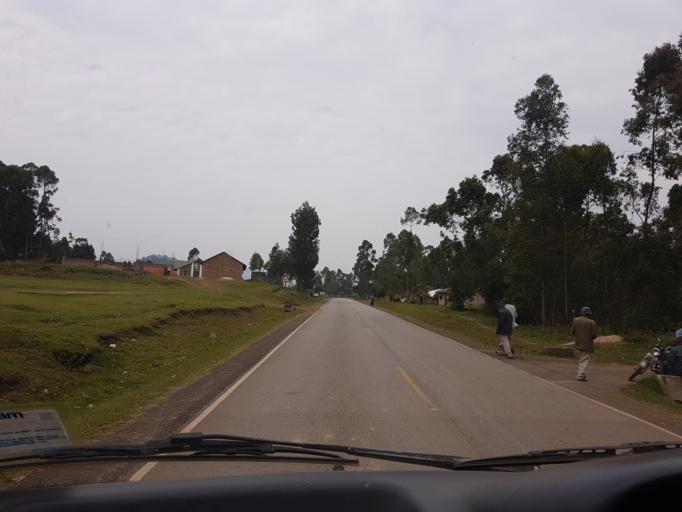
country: UG
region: Western Region
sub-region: Kisoro District
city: Kisoro
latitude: -1.3136
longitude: 29.7220
